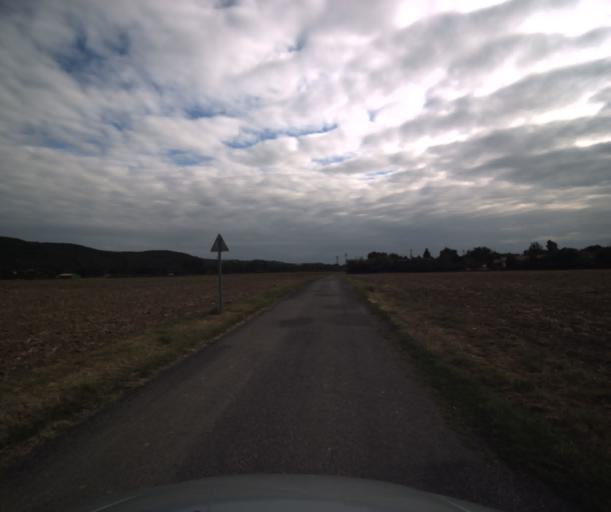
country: FR
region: Midi-Pyrenees
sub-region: Departement de la Haute-Garonne
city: Le Fauga
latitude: 43.4311
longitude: 1.3127
